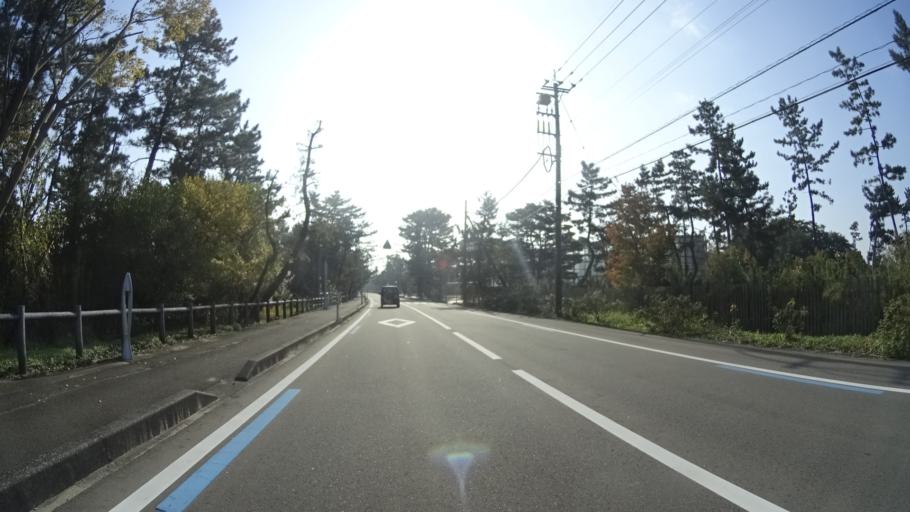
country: JP
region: Toyama
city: Himi
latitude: 36.8382
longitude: 137.0040
